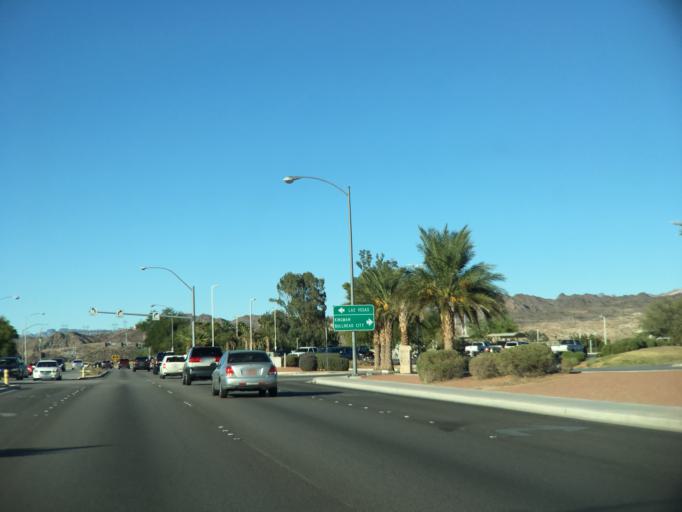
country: US
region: Nevada
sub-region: Clark County
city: Laughlin
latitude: 35.1694
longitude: -114.5720
